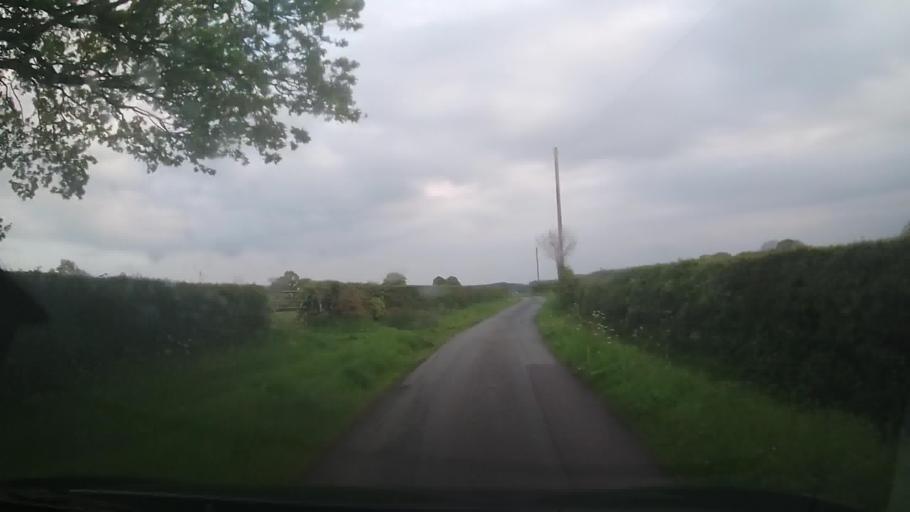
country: GB
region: England
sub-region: Shropshire
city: Ellesmere
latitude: 52.9362
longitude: -2.8609
